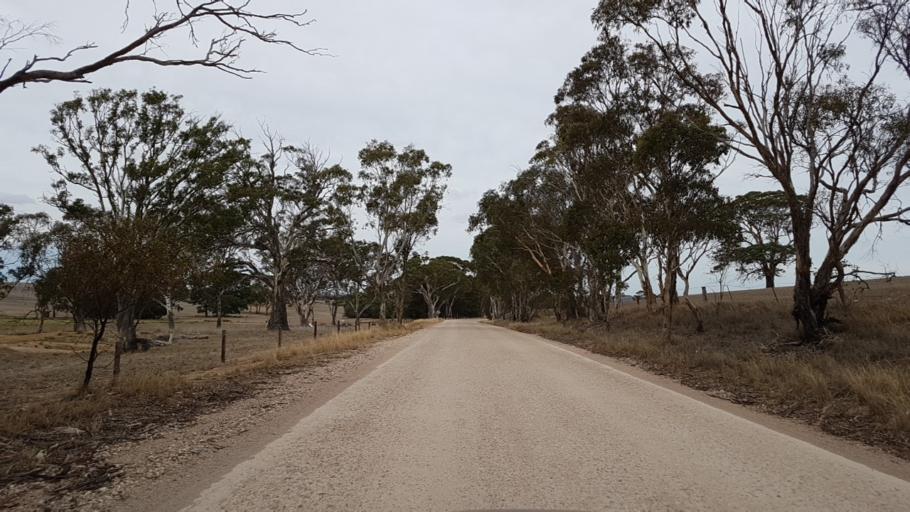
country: AU
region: South Australia
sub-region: Adelaide Hills
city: Birdwood
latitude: -34.9341
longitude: 139.0755
